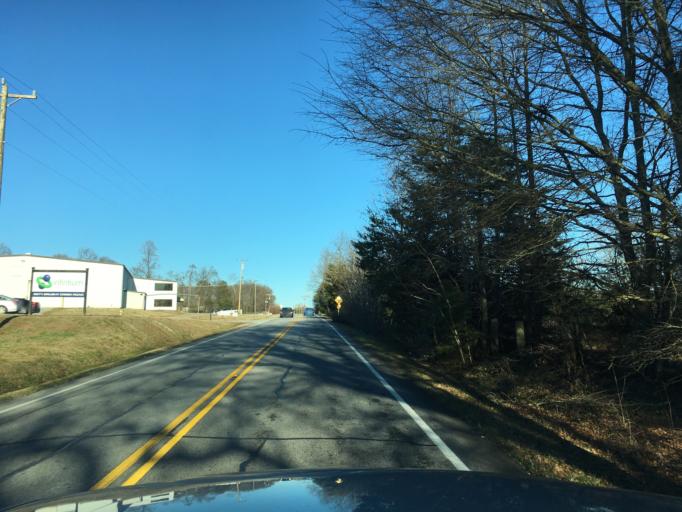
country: US
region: South Carolina
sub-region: Greenville County
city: Taylors
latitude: 34.9194
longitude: -82.2591
